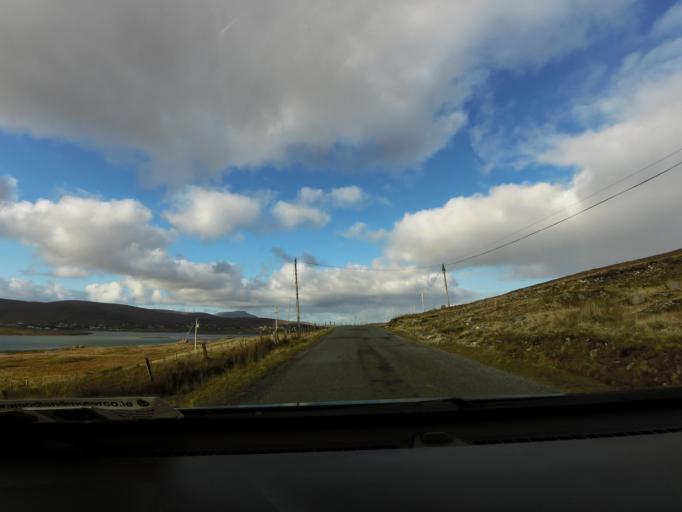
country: IE
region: Connaught
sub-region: Maigh Eo
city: Belmullet
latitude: 53.9015
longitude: -9.9209
